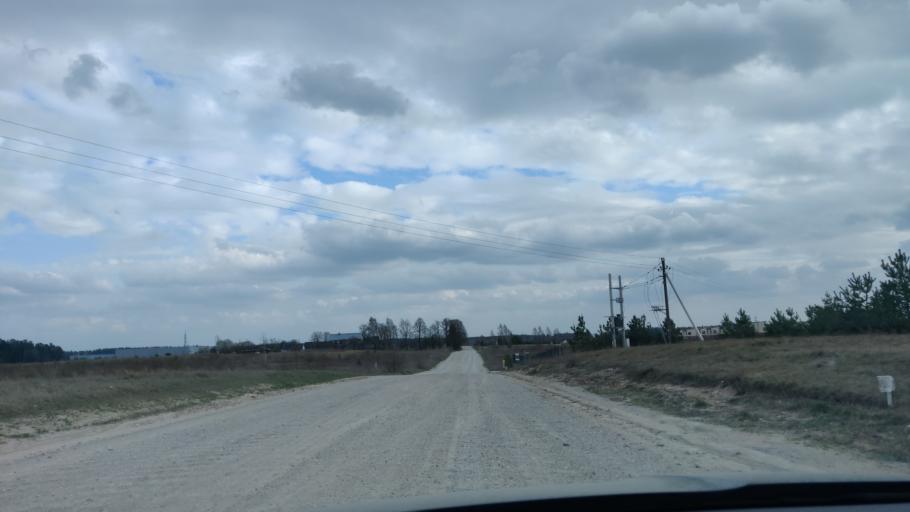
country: LT
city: Lentvaris
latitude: 54.6192
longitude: 25.0665
